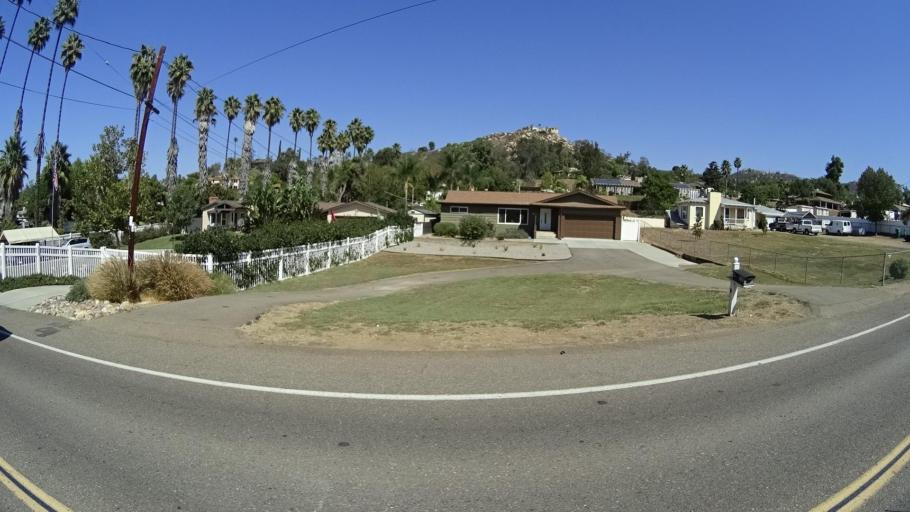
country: US
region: California
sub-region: San Diego County
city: Granite Hills
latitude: 32.8055
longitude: -116.9091
